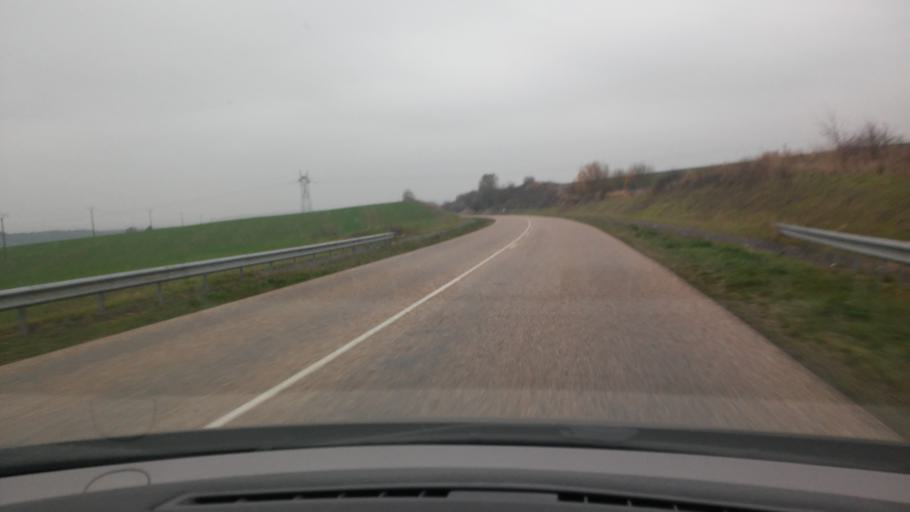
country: FR
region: Lorraine
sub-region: Departement de la Moselle
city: Boulay-Moselle
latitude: 49.1504
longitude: 6.4847
